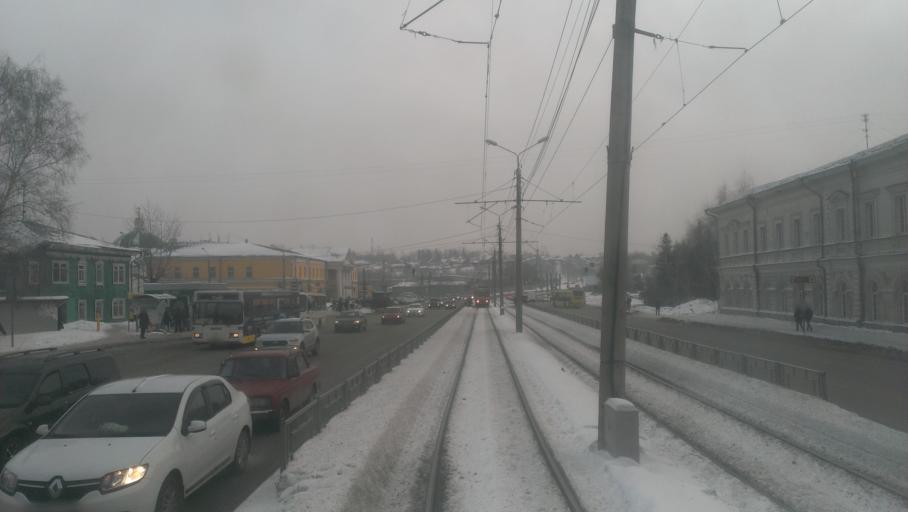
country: RU
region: Altai Krai
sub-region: Gorod Barnaulskiy
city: Barnaul
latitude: 53.3301
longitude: 83.7834
